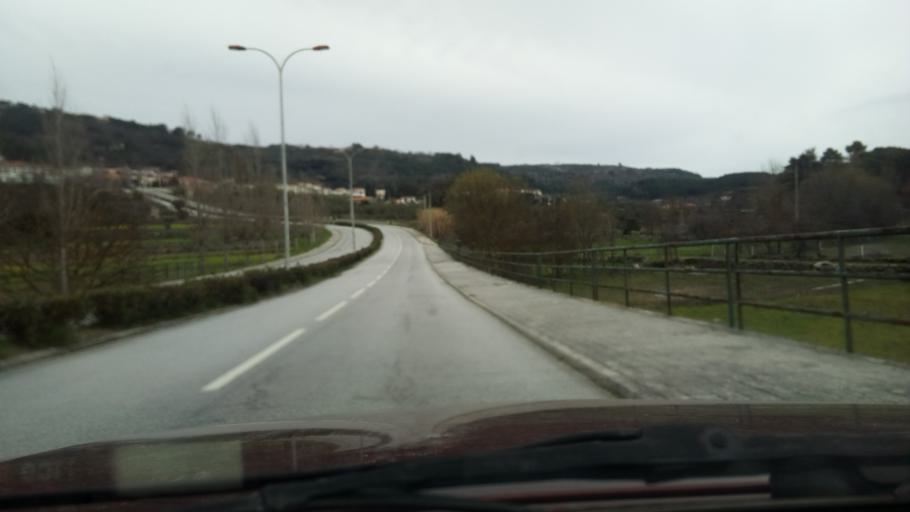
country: PT
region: Guarda
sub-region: Fornos de Algodres
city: Fornos de Algodres
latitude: 40.6154
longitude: -7.5339
